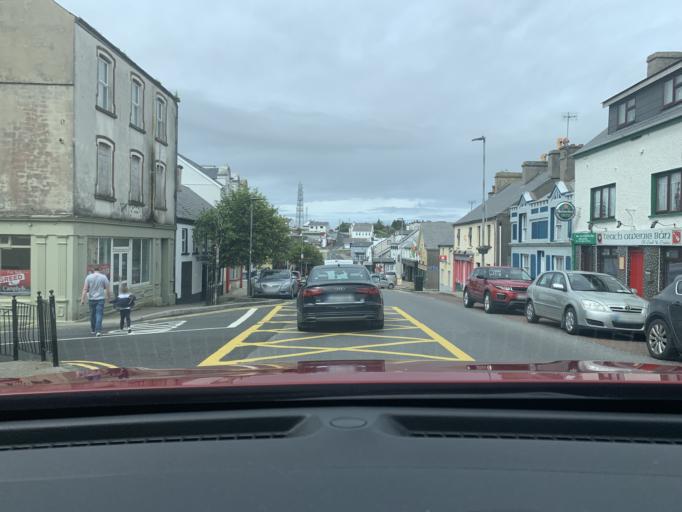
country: IE
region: Ulster
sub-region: County Donegal
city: Dungloe
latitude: 54.9493
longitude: -8.3604
